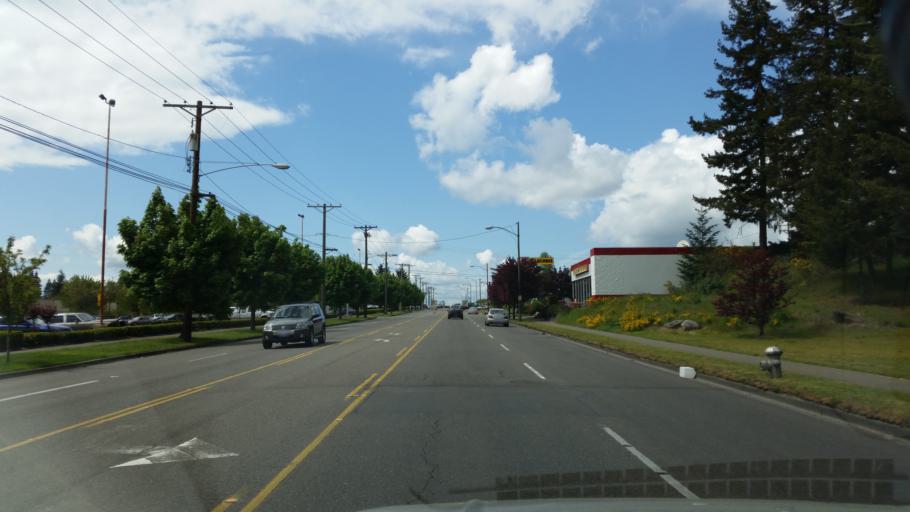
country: US
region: Washington
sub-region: Pierce County
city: Fircrest
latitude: 47.2554
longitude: -122.5065
